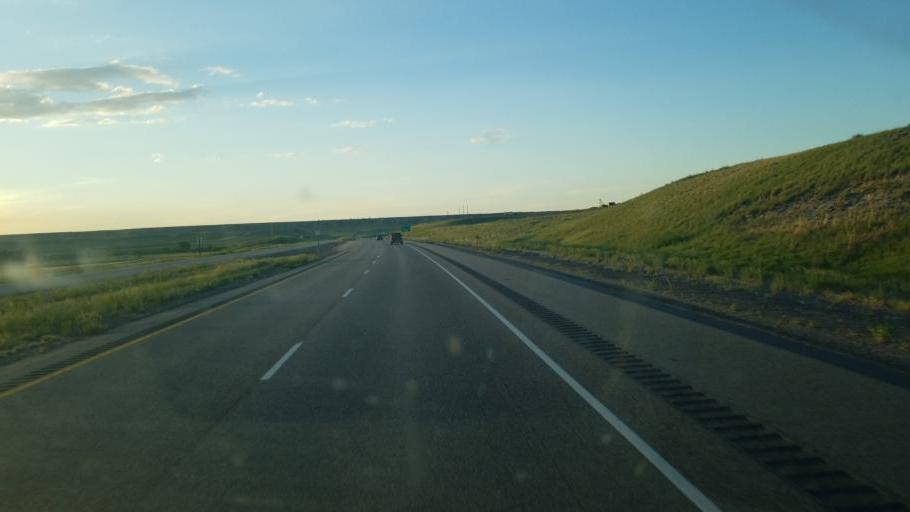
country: US
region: Wyoming
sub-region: Platte County
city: Wheatland
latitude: 41.7360
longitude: -104.8287
